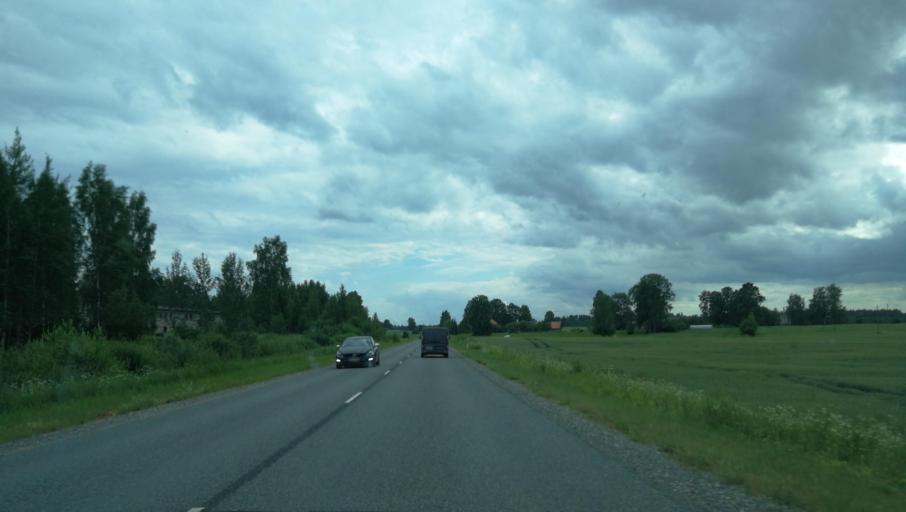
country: LV
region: Naukseni
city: Naukseni
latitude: 57.7430
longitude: 25.4304
